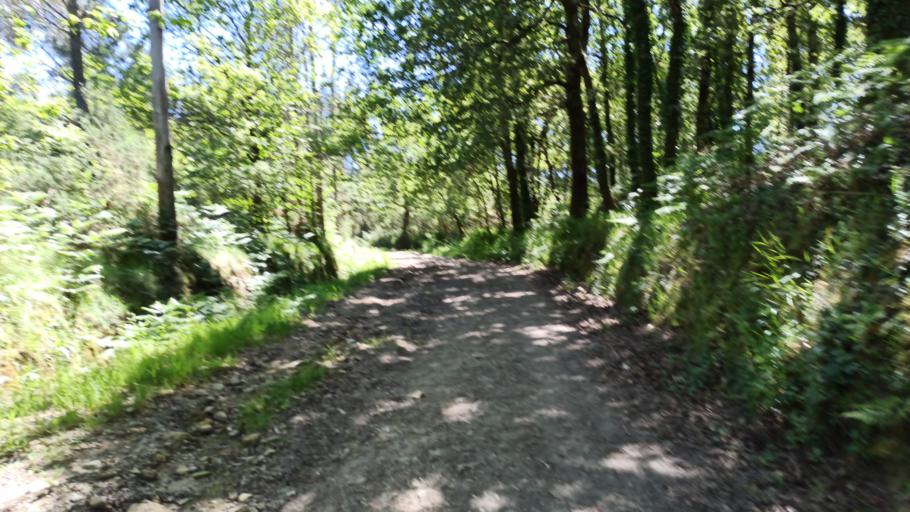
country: ES
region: Galicia
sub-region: Provincia da Coruna
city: Negreira
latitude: 42.9181
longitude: -8.7269
